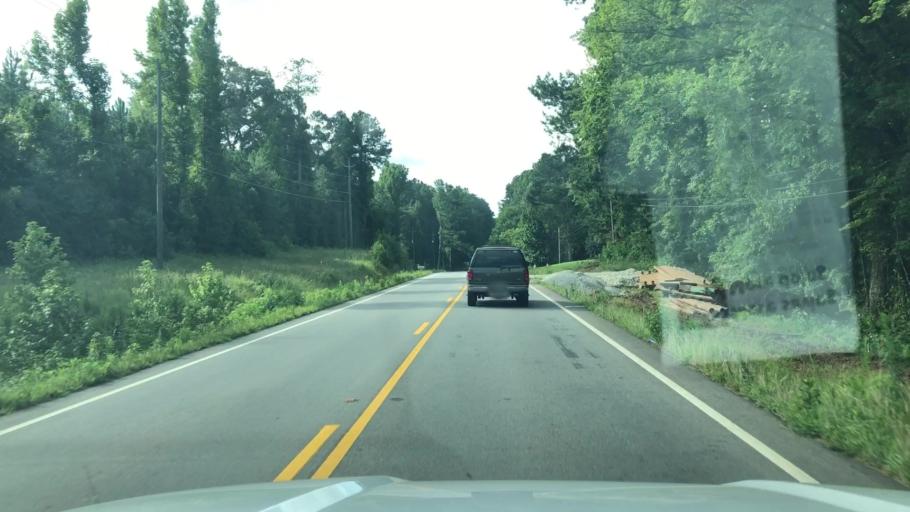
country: US
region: Georgia
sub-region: Paulding County
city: Dallas
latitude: 33.9444
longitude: -84.8468
